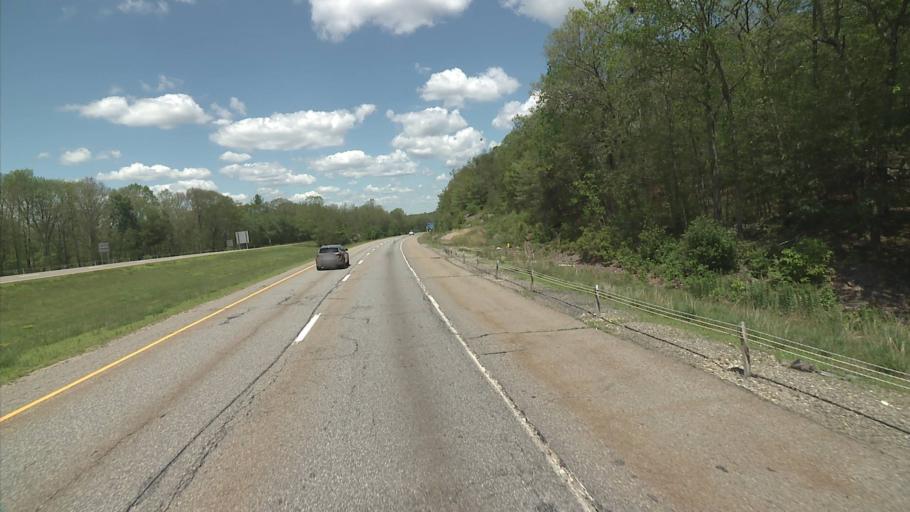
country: US
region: Massachusetts
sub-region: Worcester County
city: Webster
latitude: 42.0227
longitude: -71.8602
